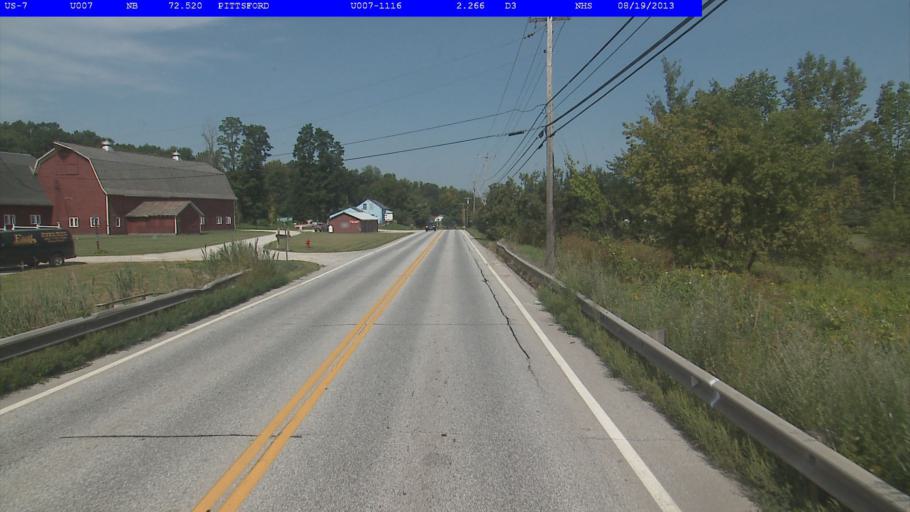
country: US
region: Vermont
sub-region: Rutland County
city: Rutland
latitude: 43.6948
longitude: -73.0026
